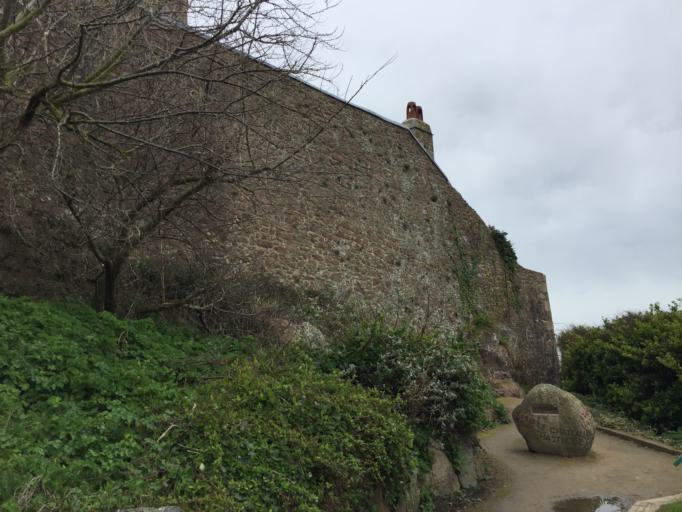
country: JE
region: St Helier
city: Saint Helier
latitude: 49.1992
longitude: -2.0199
